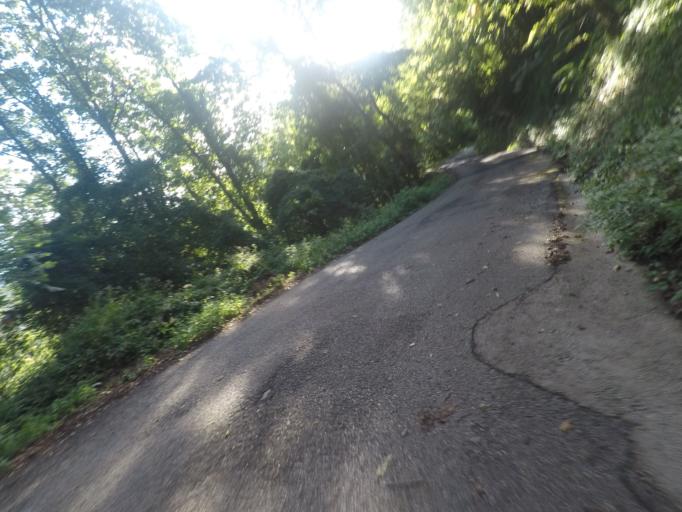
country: IT
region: Tuscany
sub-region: Provincia di Lucca
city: Pescaglia
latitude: 43.9408
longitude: 10.3945
